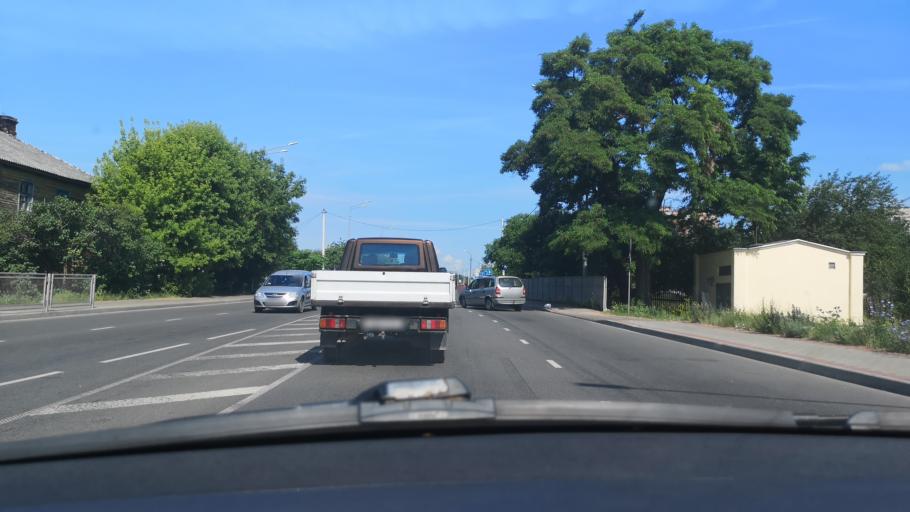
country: BY
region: Brest
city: Brest
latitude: 52.1049
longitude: 23.7172
